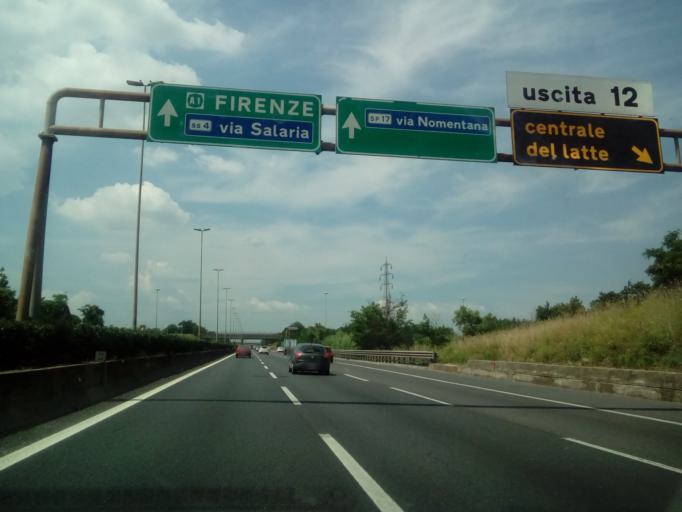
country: IT
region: Latium
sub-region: Citta metropolitana di Roma Capitale
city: Colle Verde
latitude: 41.9423
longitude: 12.5943
